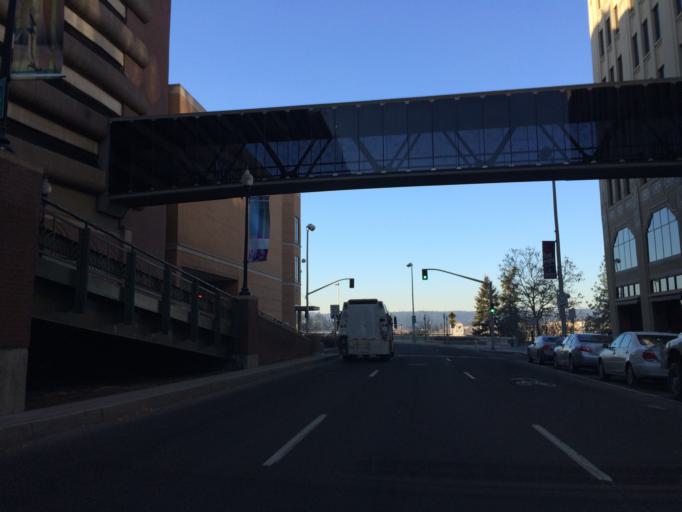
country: US
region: Washington
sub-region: Spokane County
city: Spokane
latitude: 47.6601
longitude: -117.4237
